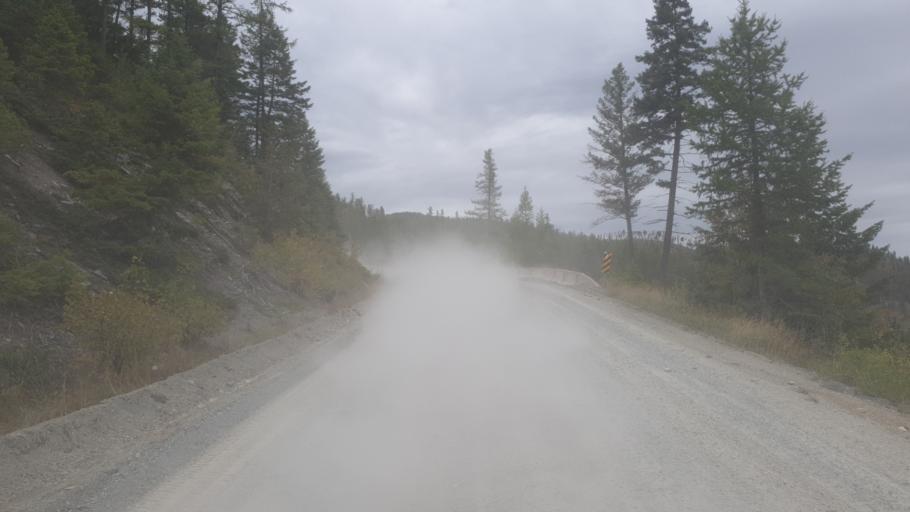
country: US
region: Montana
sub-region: Flathead County
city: Lakeside
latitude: 47.9892
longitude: -114.3161
